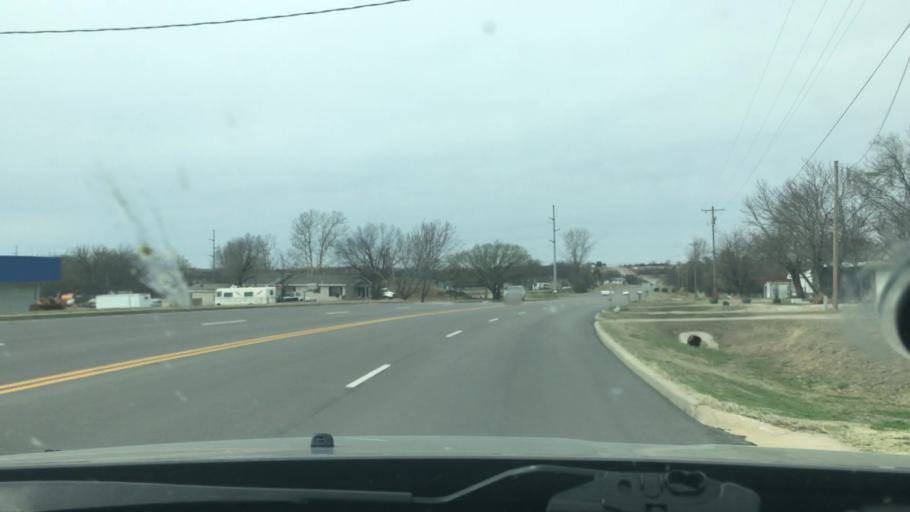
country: US
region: Oklahoma
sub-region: Seminole County
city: Seminole
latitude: 35.2613
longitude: -96.7134
